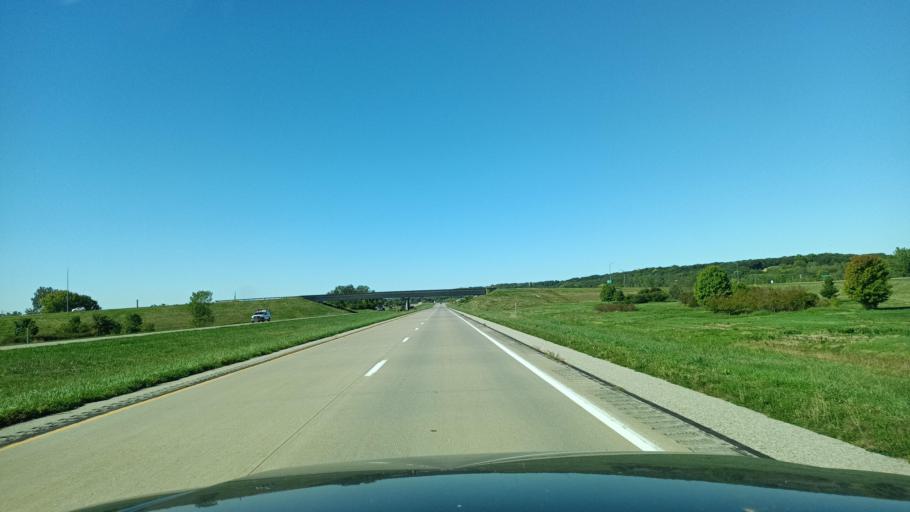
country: US
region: Illinois
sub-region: Hancock County
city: Nauvoo
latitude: 40.6276
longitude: -91.3953
